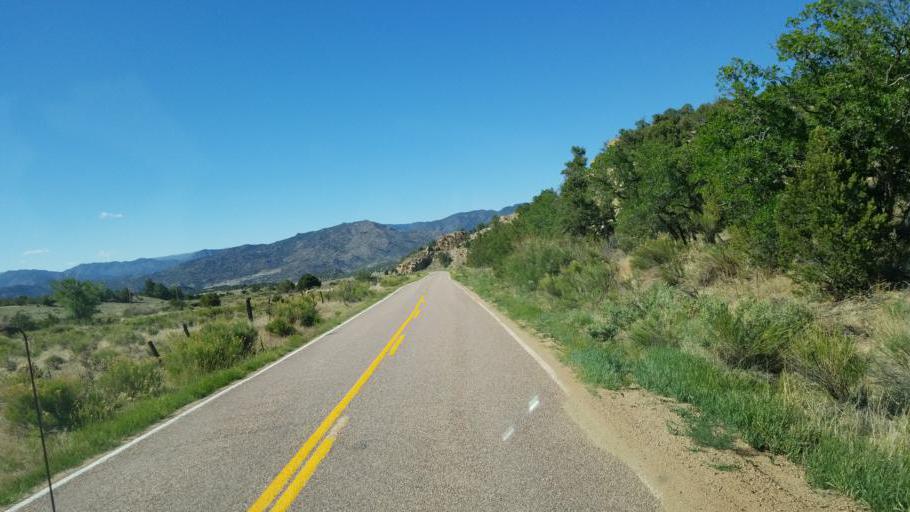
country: US
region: Colorado
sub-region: Fremont County
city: Canon City
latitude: 38.4452
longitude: -105.3735
